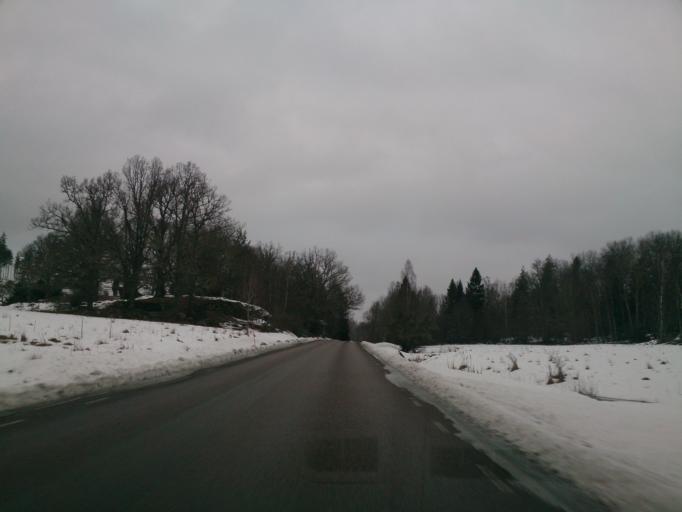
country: SE
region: OEstergoetland
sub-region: Atvidabergs Kommun
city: Atvidaberg
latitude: 58.2615
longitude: 16.0263
